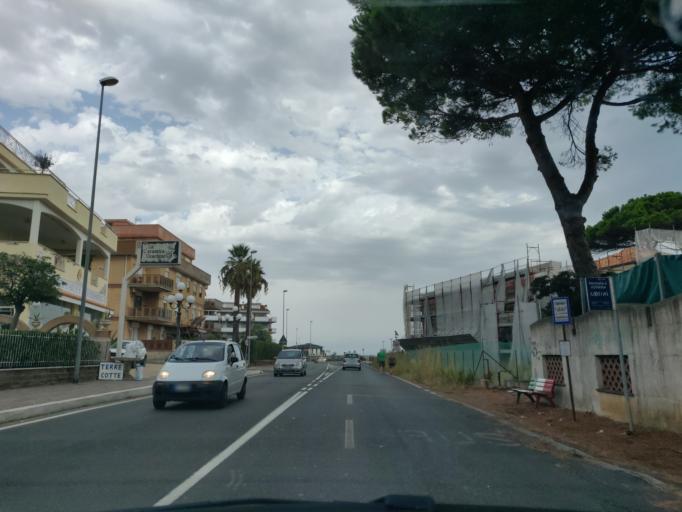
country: IT
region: Latium
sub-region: Citta metropolitana di Roma Capitale
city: Santa Marinella
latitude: 42.0399
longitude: 11.8851
